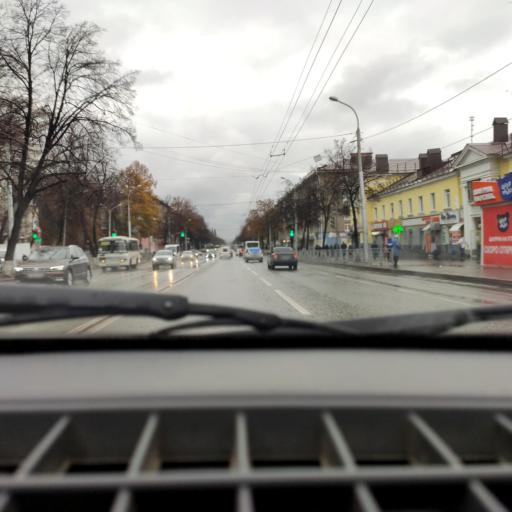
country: RU
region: Bashkortostan
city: Ufa
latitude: 54.8153
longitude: 56.0829
